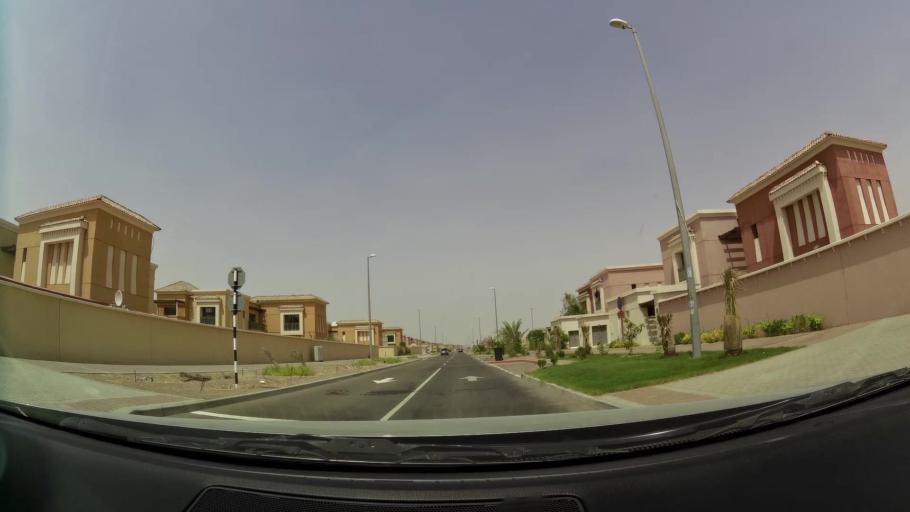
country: AE
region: Abu Dhabi
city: Al Ain
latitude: 24.1474
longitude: 55.6285
